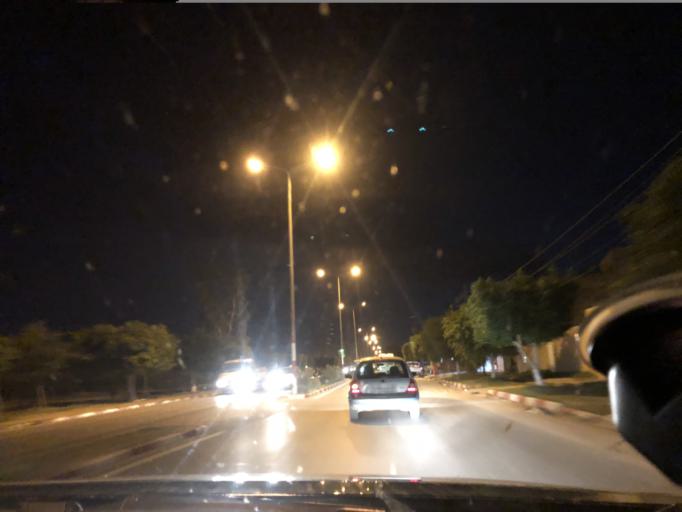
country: TN
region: Al Qasrayn
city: Kasserine
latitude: 35.1823
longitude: 8.8591
